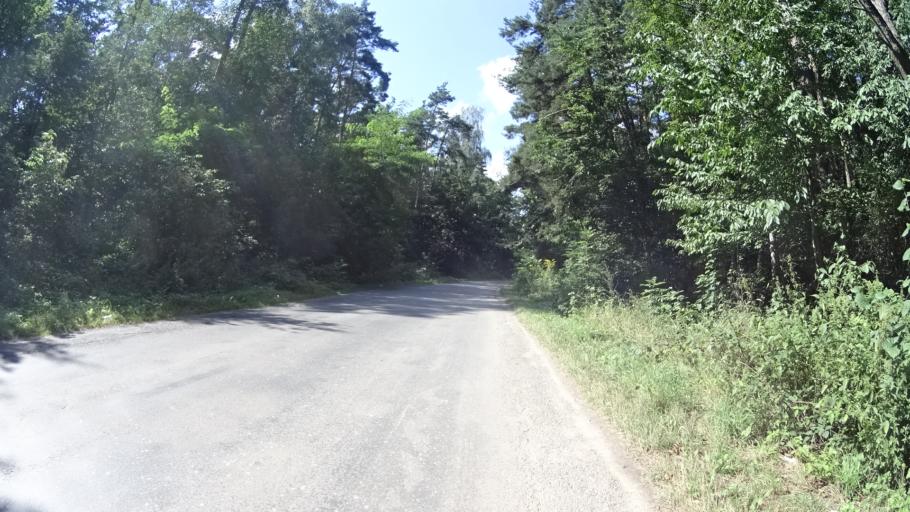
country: PL
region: Masovian Voivodeship
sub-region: Powiat grojecki
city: Mogielnica
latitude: 51.6913
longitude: 20.7401
